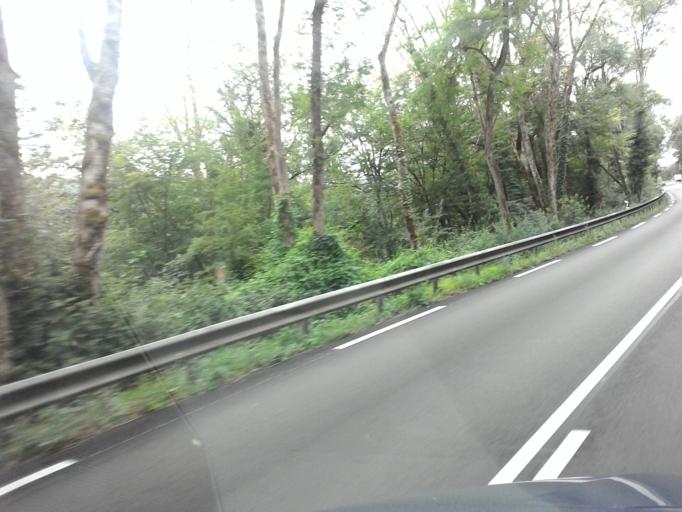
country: FR
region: Franche-Comte
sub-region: Departement du Doubs
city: Boussieres
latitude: 47.1404
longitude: 5.9305
